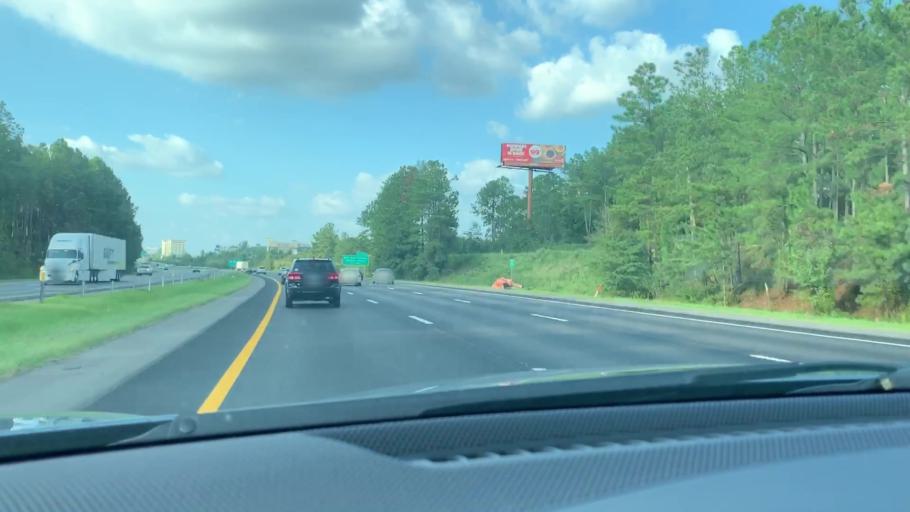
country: US
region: South Carolina
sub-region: Richland County
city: Forest Acres
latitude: 33.9621
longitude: -80.9529
